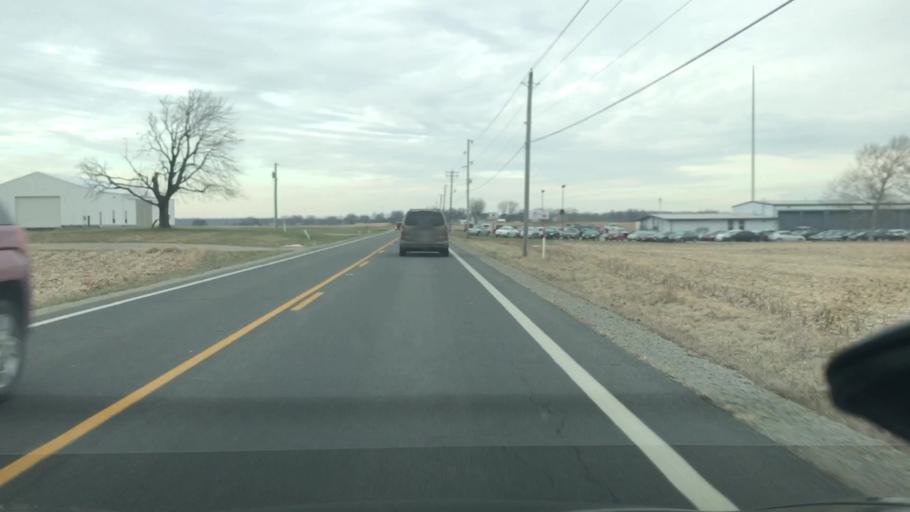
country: US
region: Ohio
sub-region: Madison County
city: Choctaw Lake
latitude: 39.9214
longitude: -83.4841
